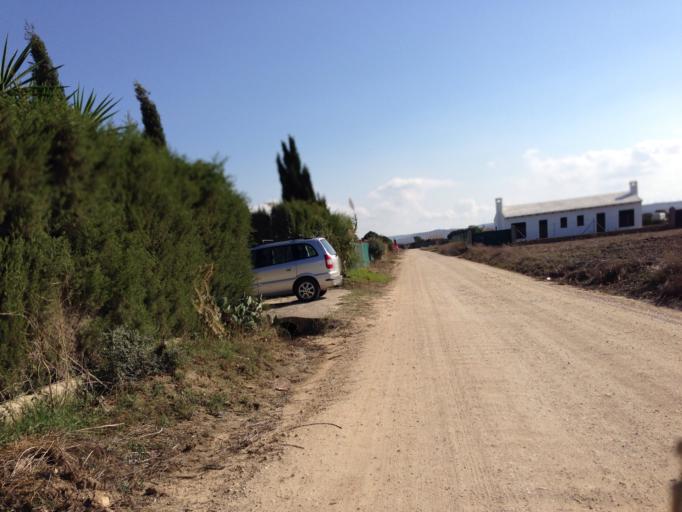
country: ES
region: Andalusia
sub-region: Provincia de Cadiz
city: Conil de la Frontera
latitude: 36.2195
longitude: -6.0551
